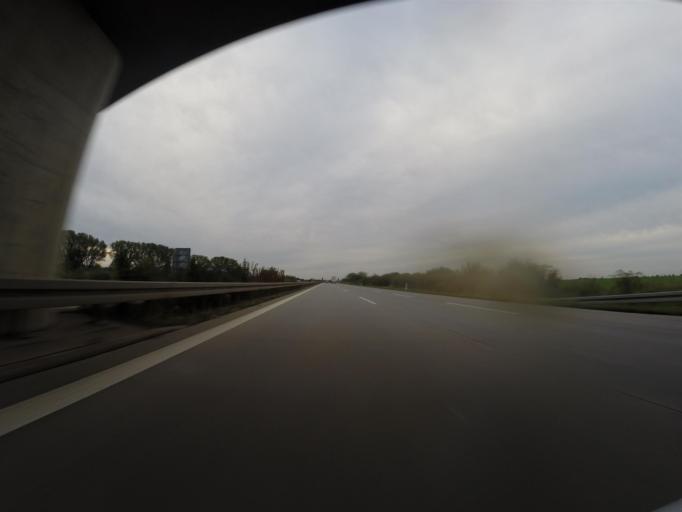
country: DE
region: Saxony
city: Kitzen
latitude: 51.2419
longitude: 12.2157
